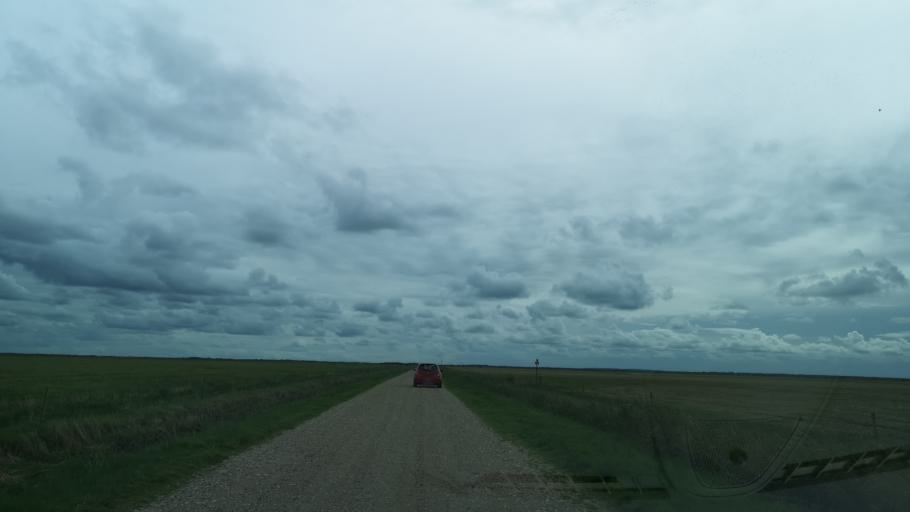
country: DK
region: Central Jutland
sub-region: Ringkobing-Skjern Kommune
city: Hvide Sande
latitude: 55.8856
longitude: 8.2197
